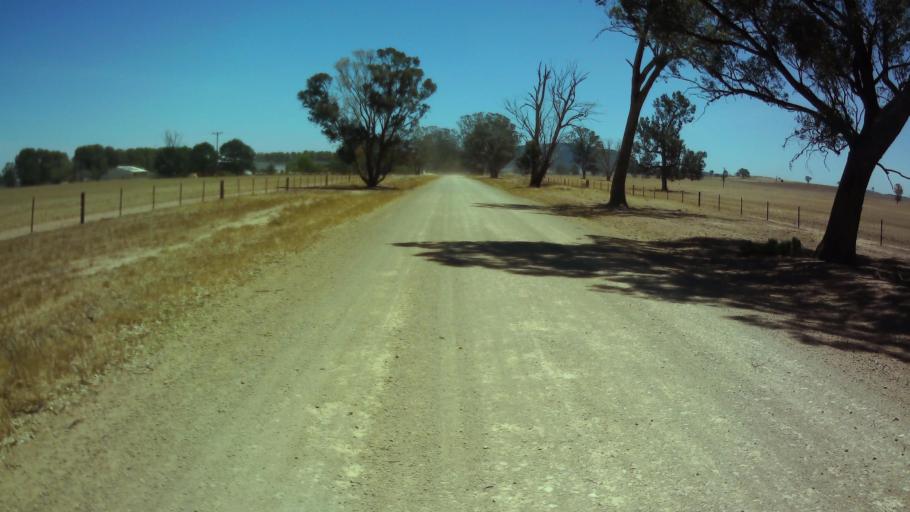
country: AU
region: New South Wales
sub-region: Weddin
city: Grenfell
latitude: -34.0115
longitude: 148.1739
